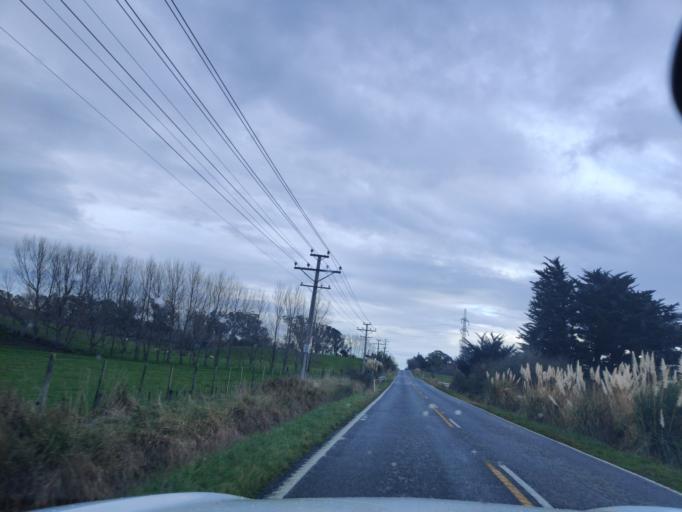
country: NZ
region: Manawatu-Wanganui
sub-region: Palmerston North City
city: Palmerston North
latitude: -40.3420
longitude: 175.7152
